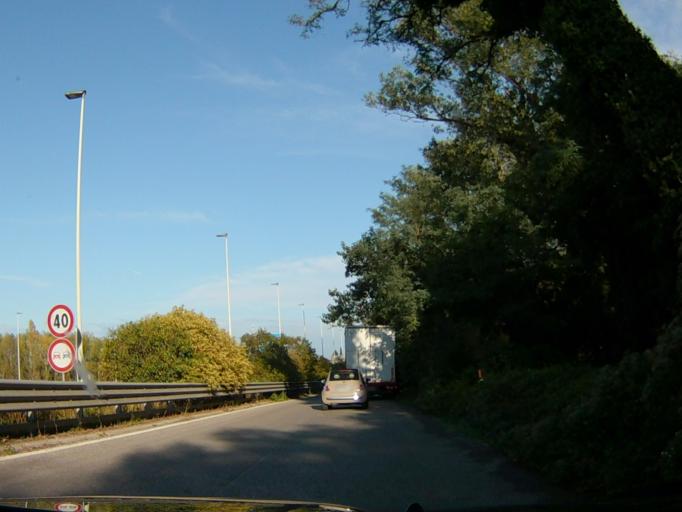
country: IT
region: Lombardy
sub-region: Provincia di Brescia
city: Desenzano del Garda
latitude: 45.4578
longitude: 10.5184
